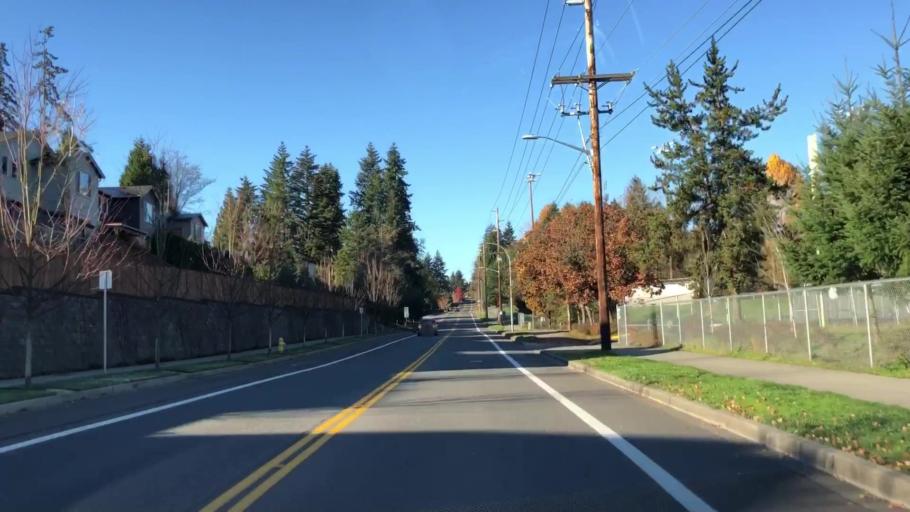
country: US
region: Washington
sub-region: King County
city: Woodinville
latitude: 47.7689
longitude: -122.1599
